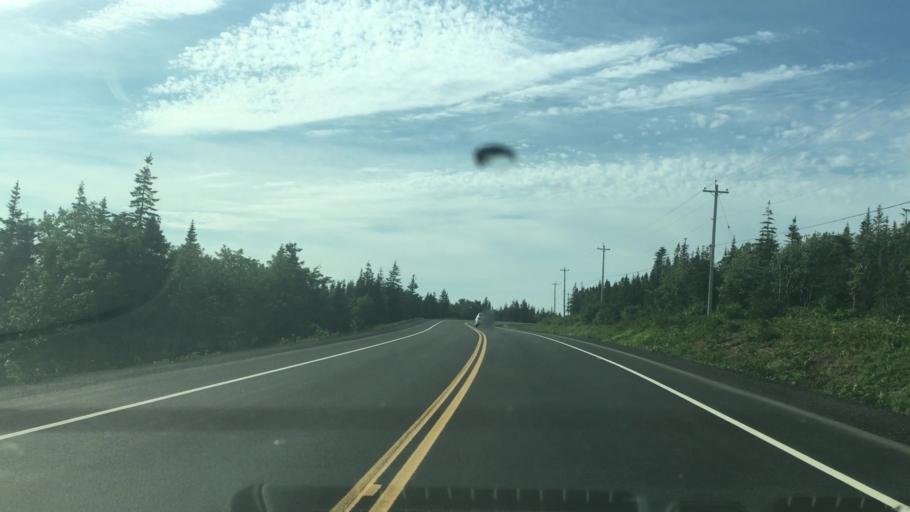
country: CA
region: Nova Scotia
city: Sydney Mines
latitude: 46.8441
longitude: -60.4049
